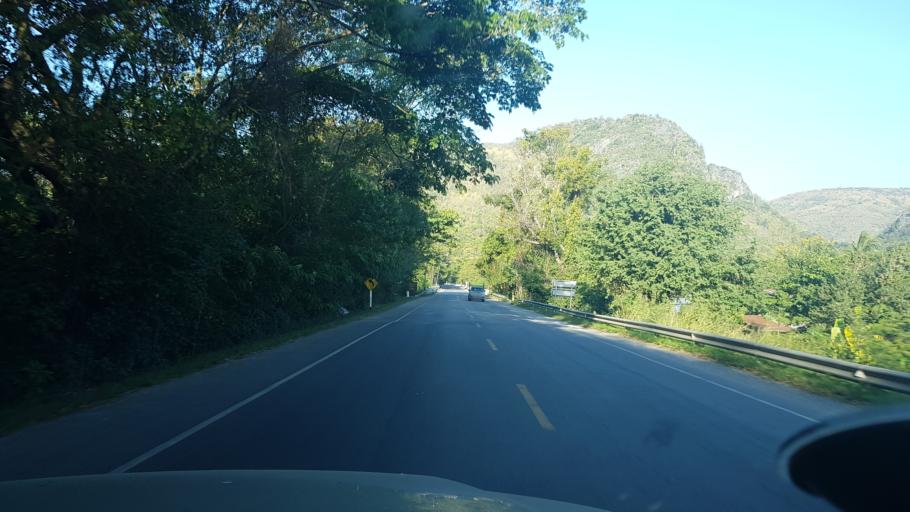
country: TH
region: Khon Kaen
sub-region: Amphoe Phu Pha Man
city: Phu Pha Man
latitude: 16.6503
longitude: 101.8074
